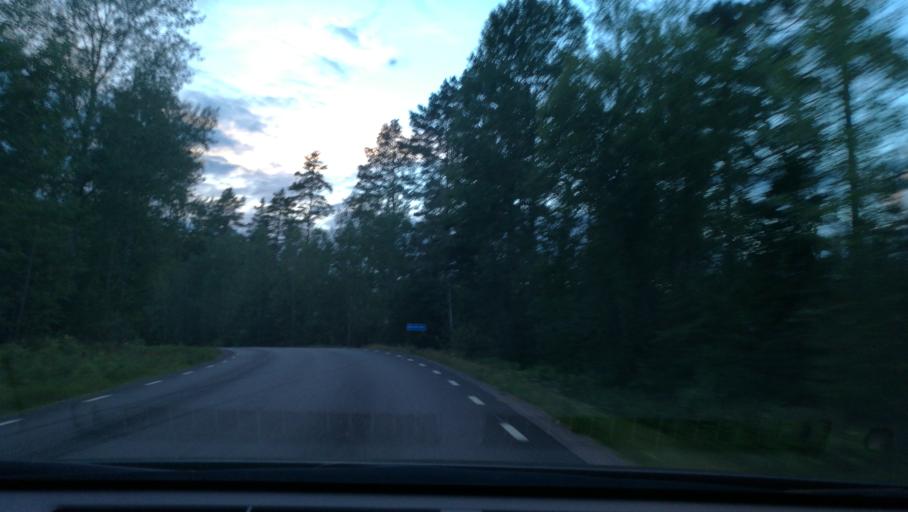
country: SE
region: OEstergoetland
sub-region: Norrkopings Kommun
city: Svartinge
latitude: 58.8276
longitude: 15.9541
